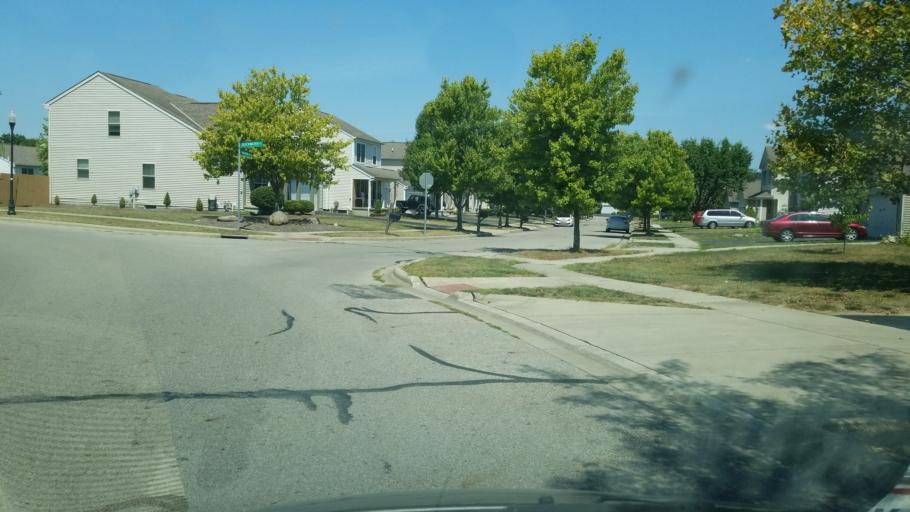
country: US
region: Ohio
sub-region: Franklin County
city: Grove City
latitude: 39.9099
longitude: -83.0897
